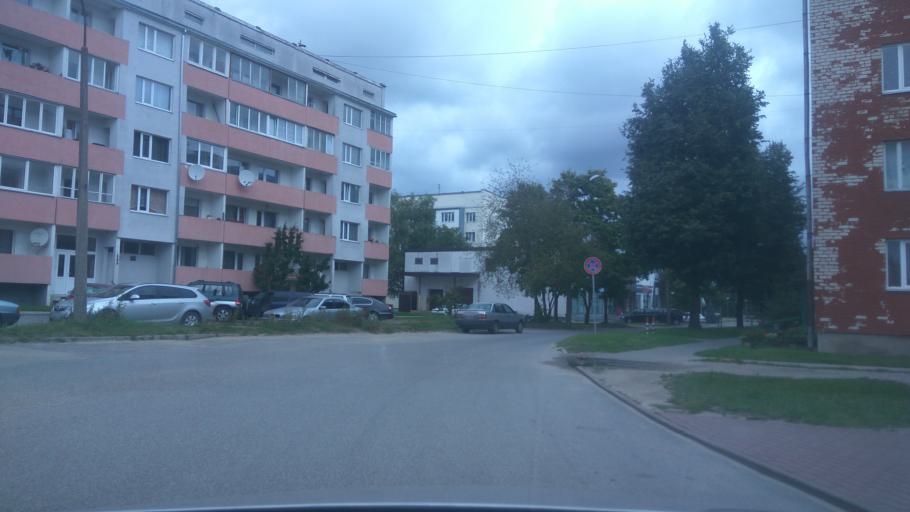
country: LV
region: Kuldigas Rajons
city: Kuldiga
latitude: 56.9735
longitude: 21.9548
